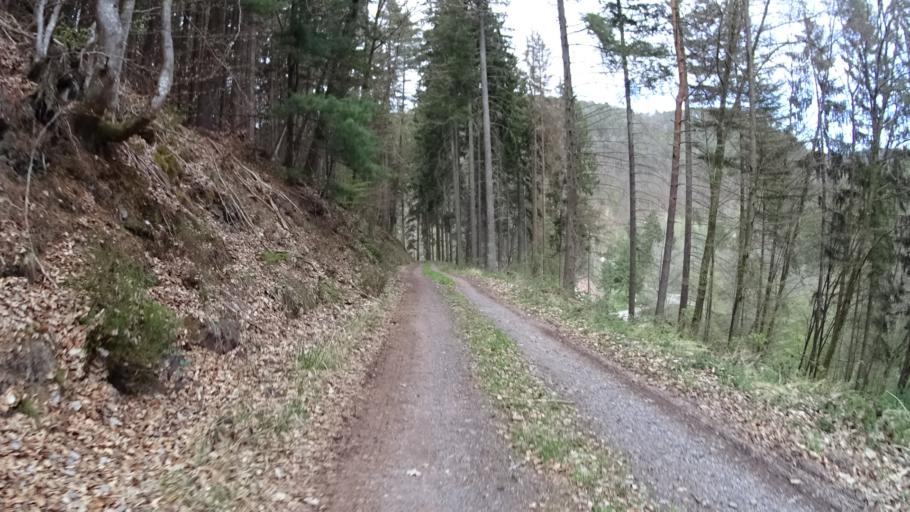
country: DE
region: Rheinland-Pfalz
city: Esthal
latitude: 49.3419
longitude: 8.0000
